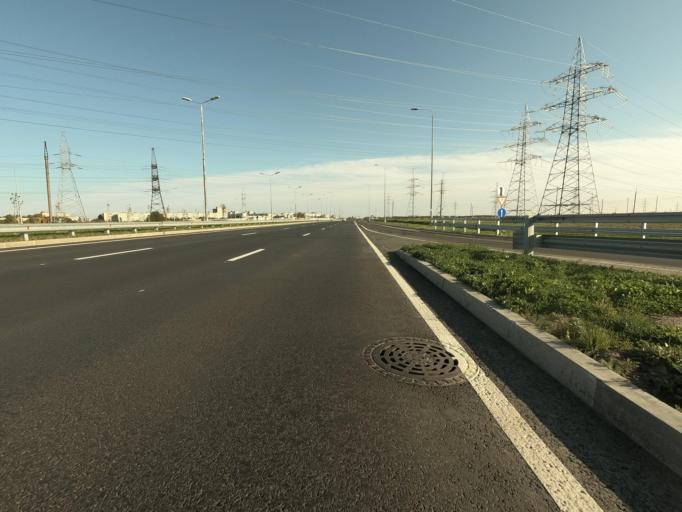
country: RU
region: St.-Petersburg
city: Kolpino
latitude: 59.7425
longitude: 30.5432
